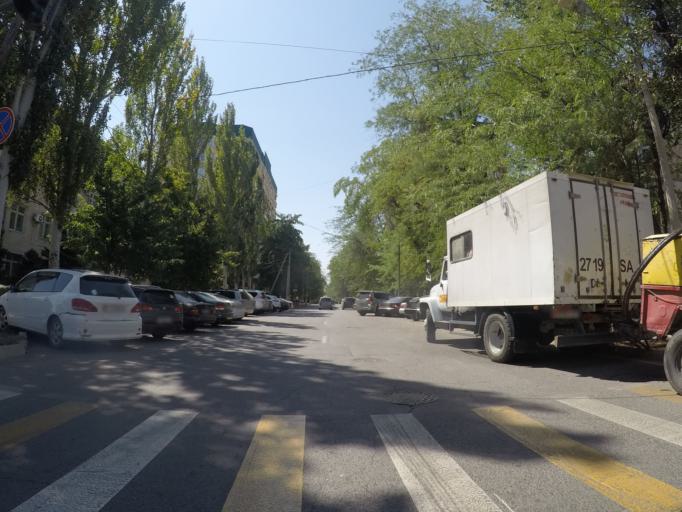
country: KG
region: Chuy
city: Bishkek
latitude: 42.8814
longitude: 74.5922
